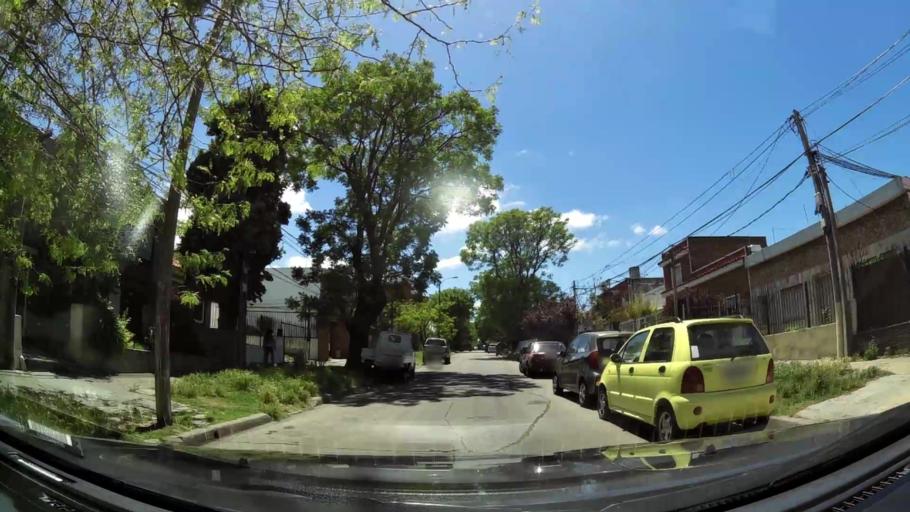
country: UY
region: Montevideo
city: Montevideo
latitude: -34.8926
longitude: -56.1292
